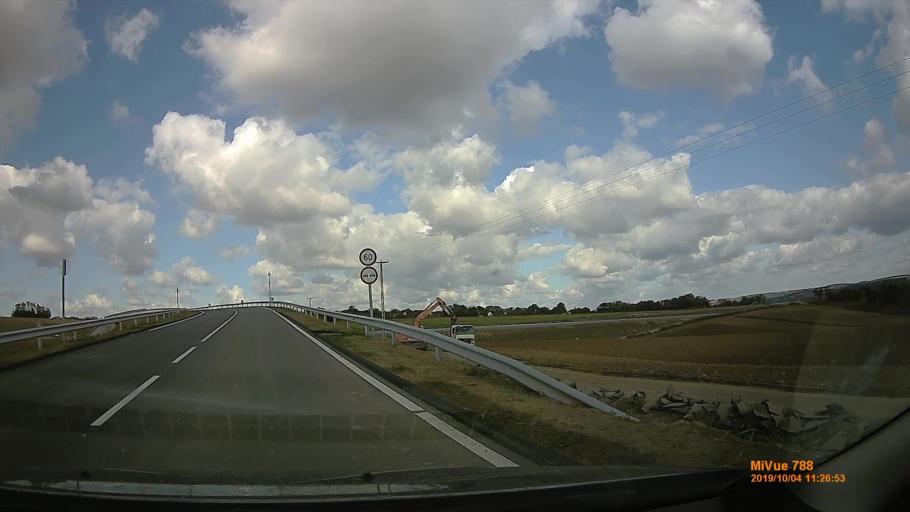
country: HU
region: Somogy
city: Kaposvar
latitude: 46.5121
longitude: 17.8114
